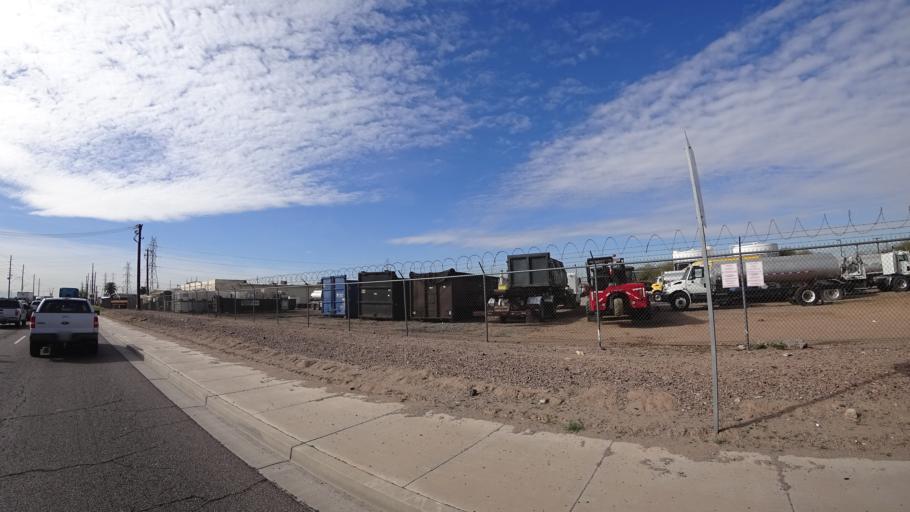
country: US
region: Arizona
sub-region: Maricopa County
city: Phoenix
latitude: 33.4461
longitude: -112.1519
